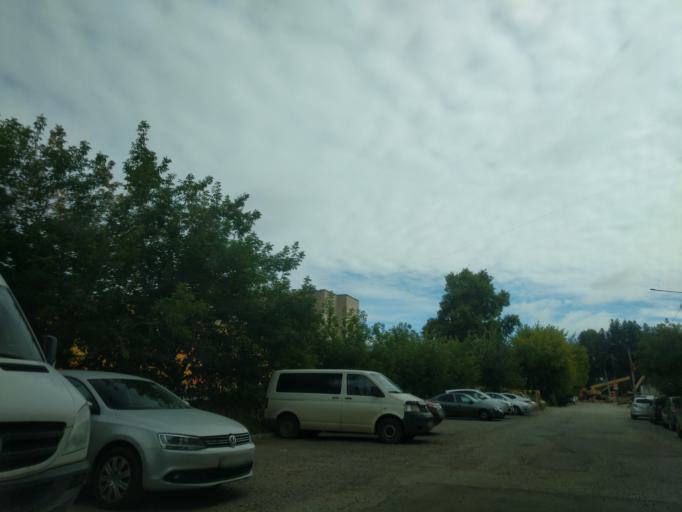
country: RU
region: Kirov
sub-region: Kirovo-Chepetskiy Rayon
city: Kirov
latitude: 58.5978
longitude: 49.6477
